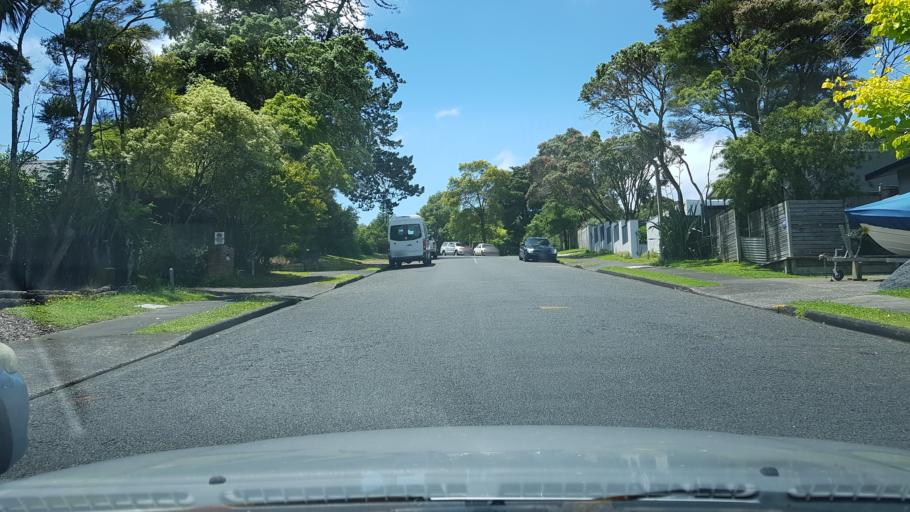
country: NZ
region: Auckland
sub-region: Auckland
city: North Shore
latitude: -36.8025
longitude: 174.7193
